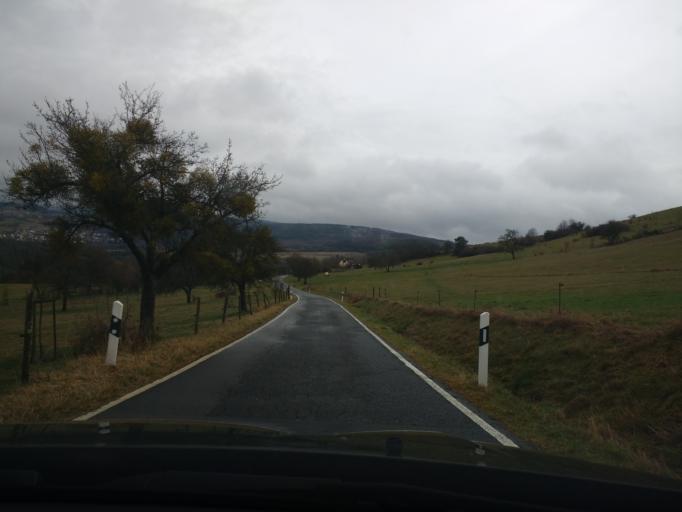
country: DE
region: Rheinland-Pfalz
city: Ollmuth
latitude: 49.6742
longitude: 6.7065
